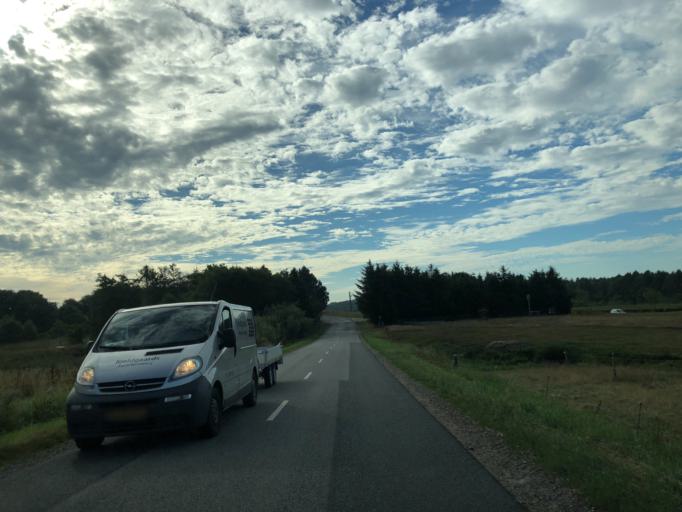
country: DK
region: Central Jutland
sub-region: Holstebro Kommune
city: Ulfborg
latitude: 56.1438
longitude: 8.4077
